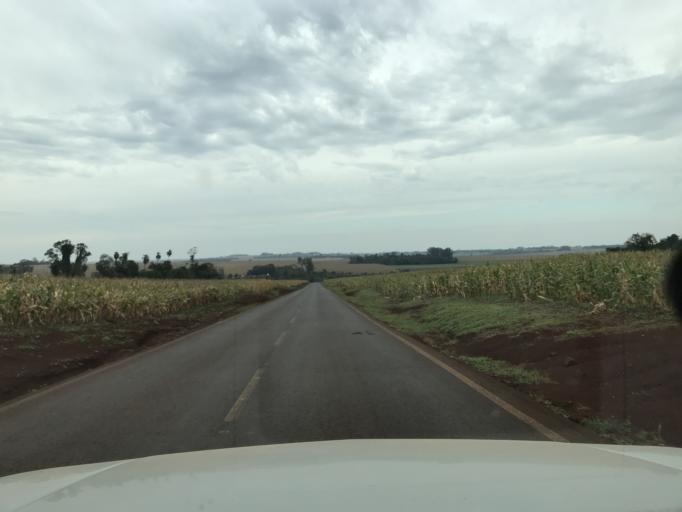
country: BR
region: Parana
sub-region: Palotina
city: Palotina
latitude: -24.4234
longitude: -53.9054
